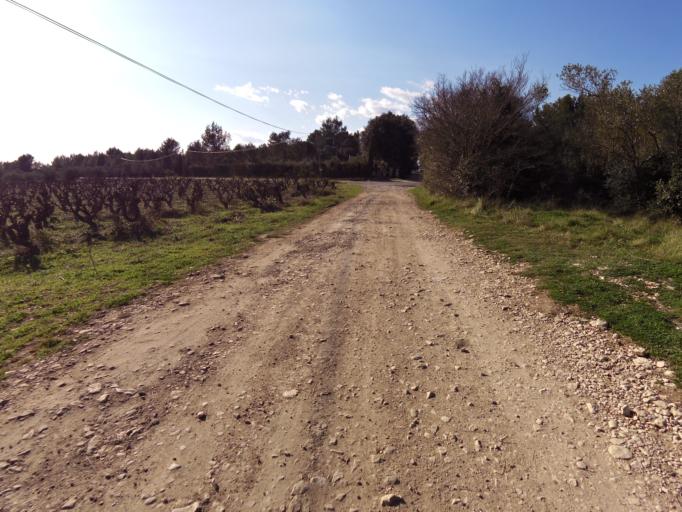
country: FR
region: Languedoc-Roussillon
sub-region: Departement du Gard
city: Congenies
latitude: 43.7628
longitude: 4.1598
